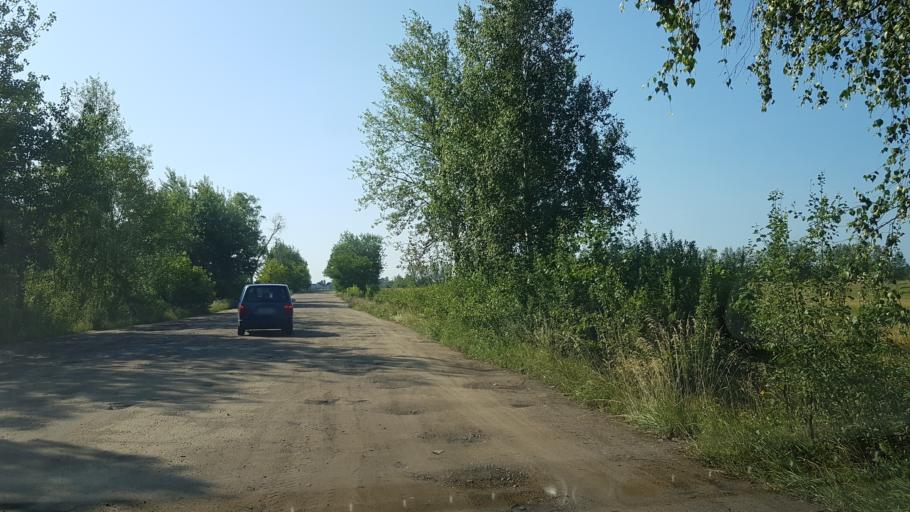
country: BY
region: Mogilev
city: Babruysk
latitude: 53.1189
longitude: 29.1876
